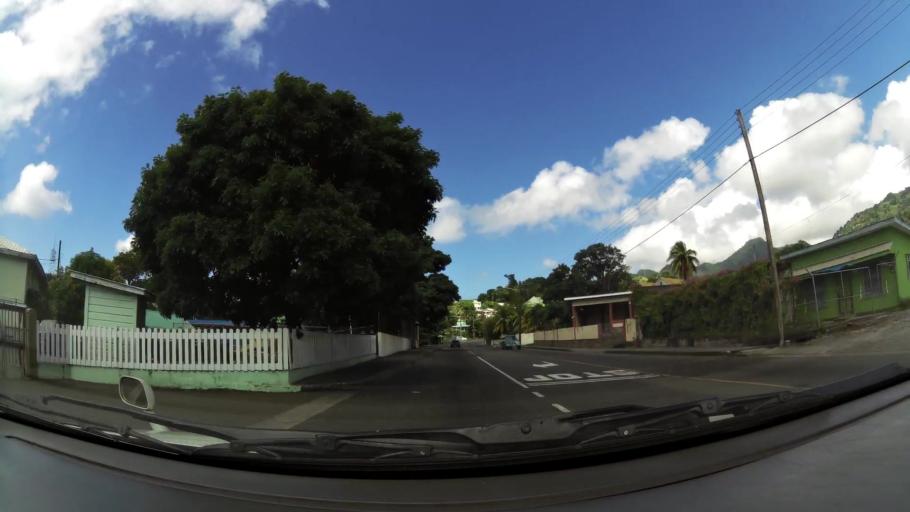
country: VC
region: Saint George
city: Kingstown
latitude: 13.1551
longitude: -61.2215
